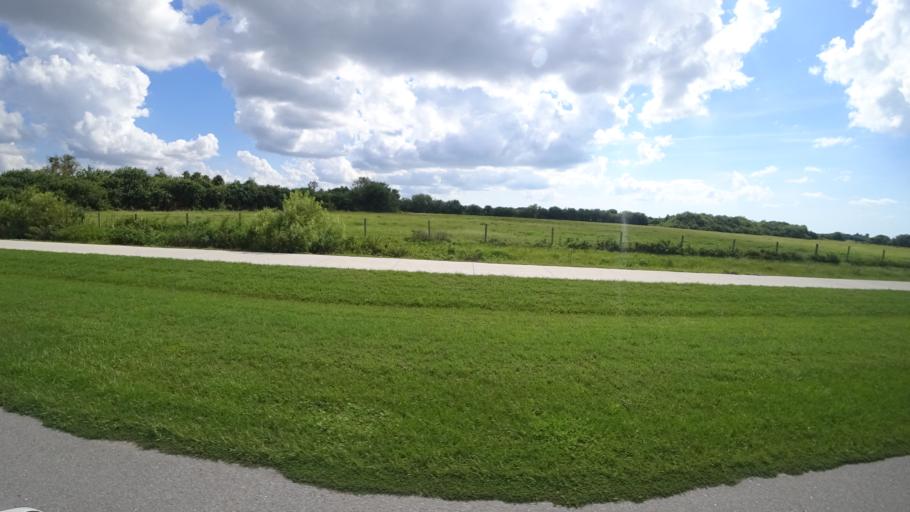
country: US
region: Florida
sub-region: Manatee County
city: Bayshore Gardens
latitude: 27.4478
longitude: -82.6179
